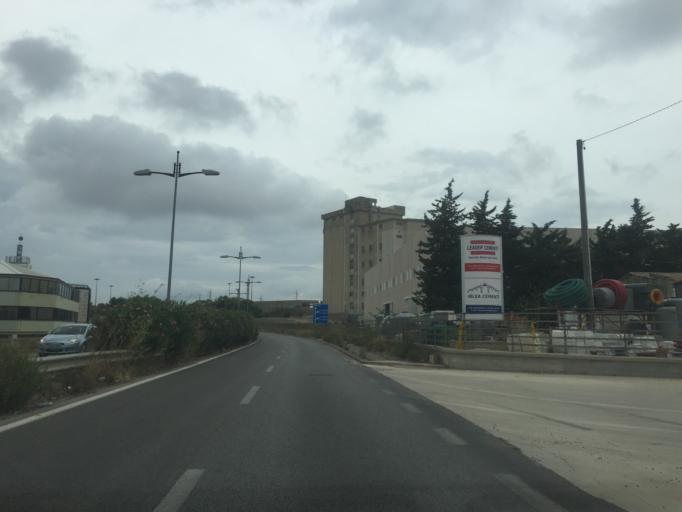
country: IT
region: Sicily
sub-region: Ragusa
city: Ragusa
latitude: 36.8903
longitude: 14.6943
